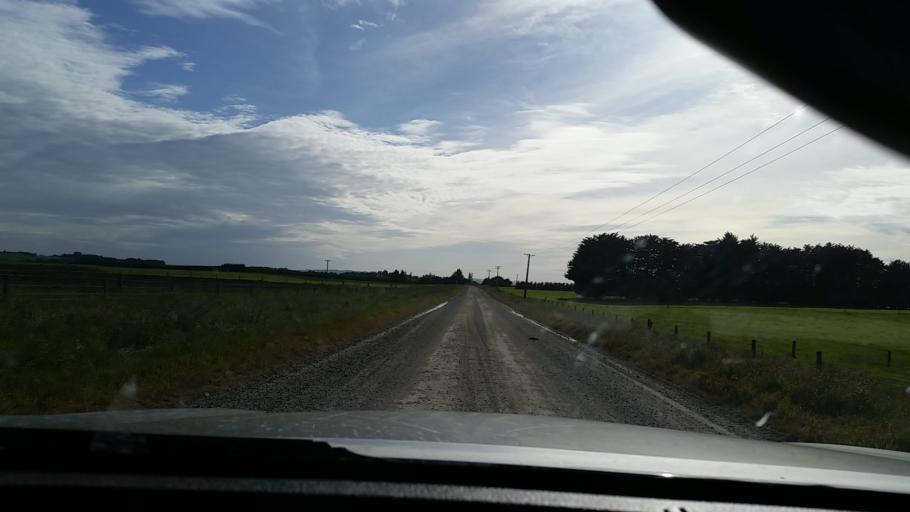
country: NZ
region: Southland
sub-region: Gore District
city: Gore
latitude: -46.2768
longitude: 168.7053
